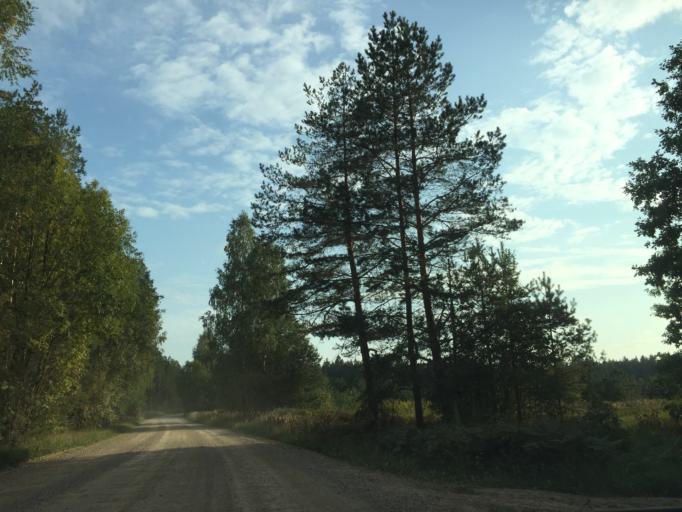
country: LV
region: Ikskile
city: Ikskile
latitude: 56.8062
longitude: 24.4410
